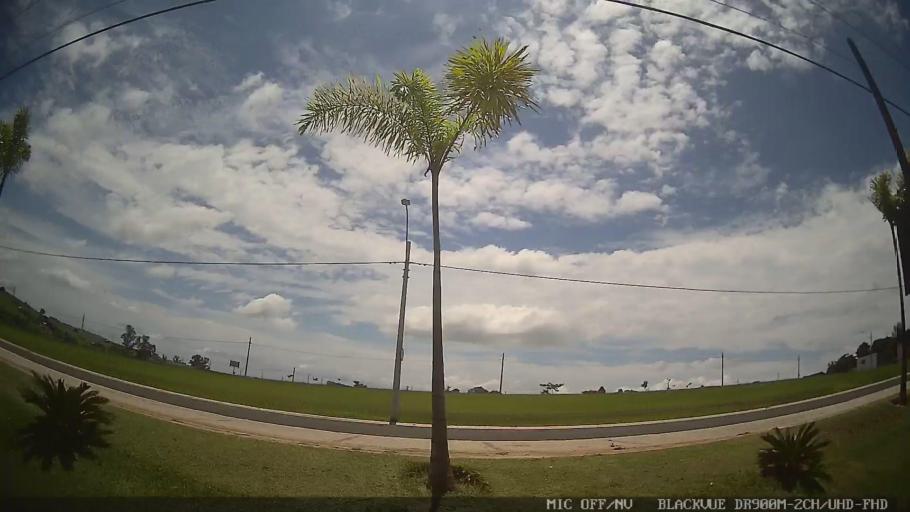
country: BR
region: Sao Paulo
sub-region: Laranjal Paulista
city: Laranjal Paulista
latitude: -23.0310
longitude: -47.8382
